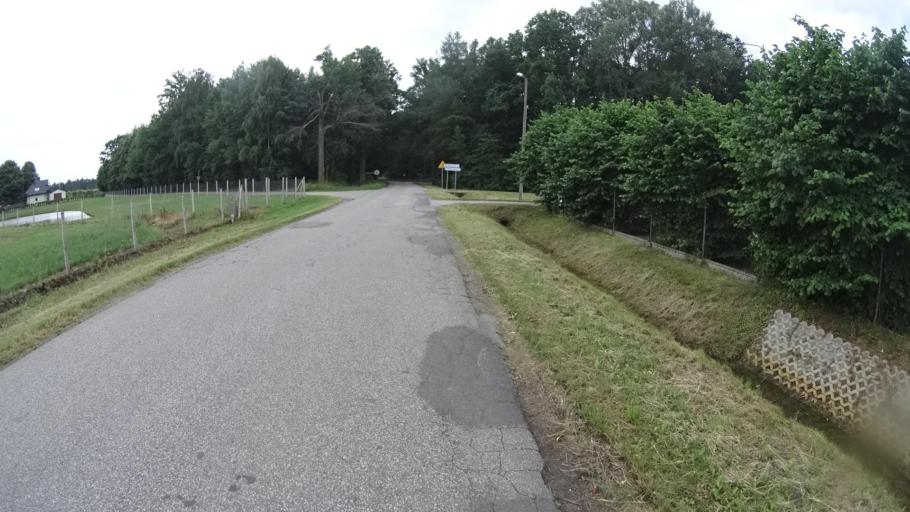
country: PL
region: Masovian Voivodeship
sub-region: Powiat grojecki
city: Goszczyn
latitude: 51.7827
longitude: 20.8543
